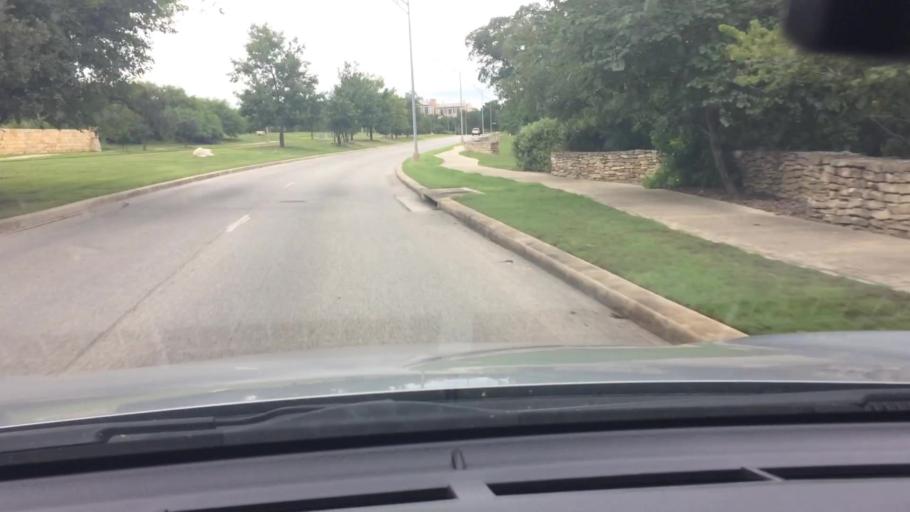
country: US
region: Texas
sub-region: Bexar County
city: Timberwood Park
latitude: 29.6527
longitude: -98.4031
